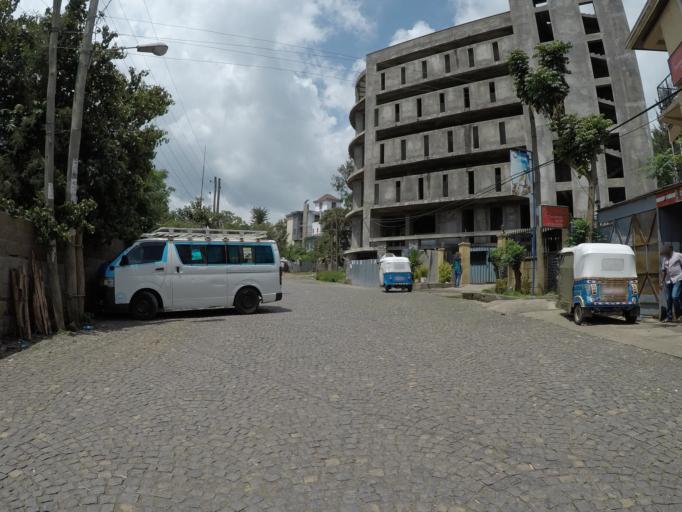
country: ET
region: Amhara
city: Gondar
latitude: 12.6139
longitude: 37.4736
